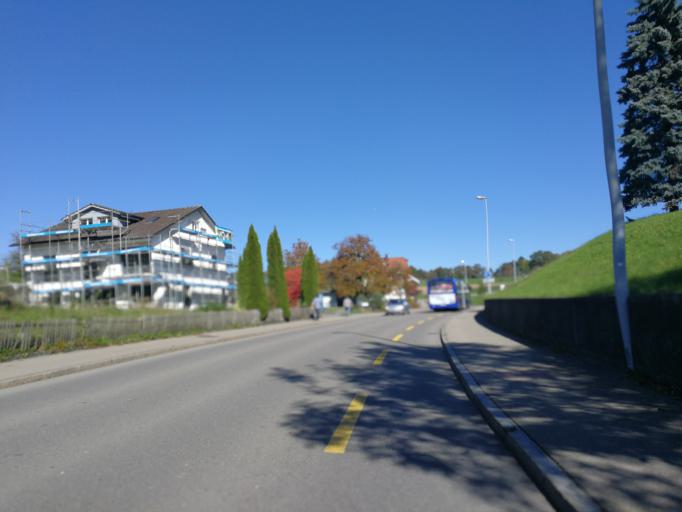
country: CH
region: Zurich
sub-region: Bezirk Hinwil
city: Gruet
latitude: 47.2949
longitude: 8.7784
